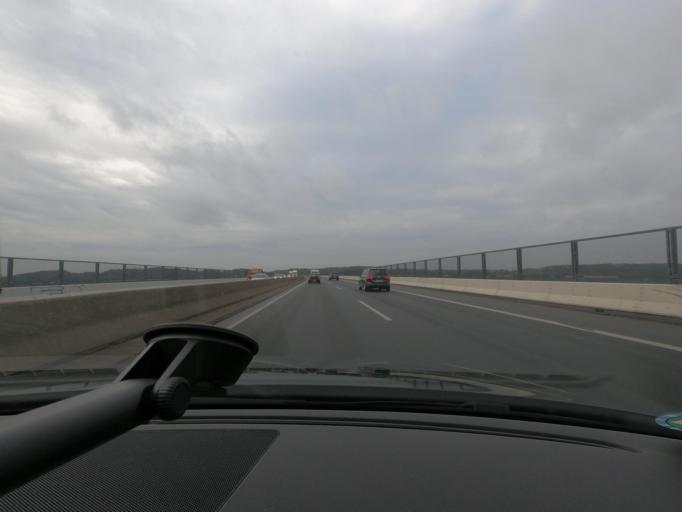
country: DE
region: North Rhine-Westphalia
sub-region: Regierungsbezirk Dusseldorf
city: Muelheim (Ruhr)
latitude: 51.3822
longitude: 6.9092
